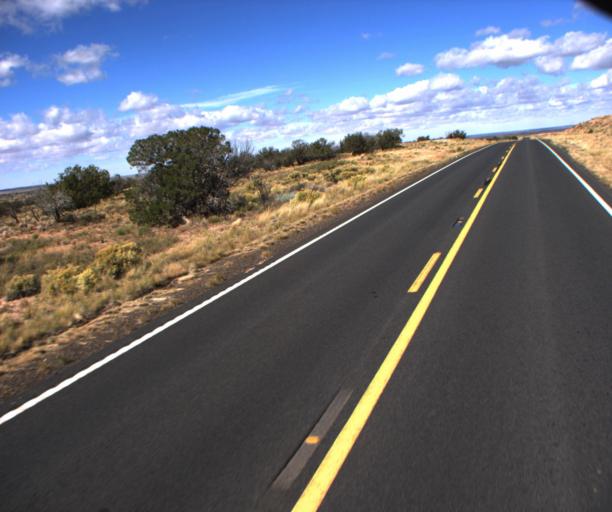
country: US
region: Arizona
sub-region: Apache County
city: Houck
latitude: 35.0767
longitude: -109.2971
